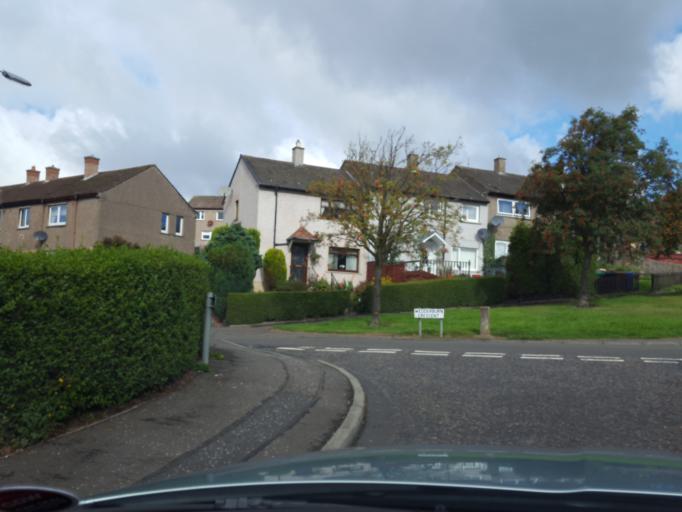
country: GB
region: Scotland
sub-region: Fife
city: Townhill
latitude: 56.0632
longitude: -3.4240
